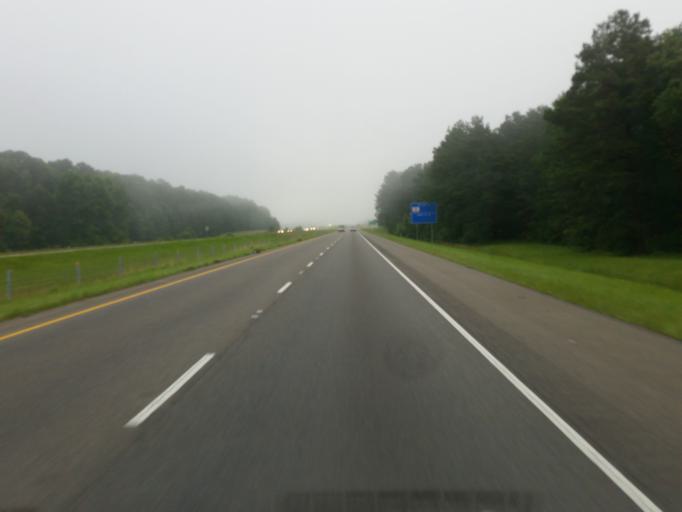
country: US
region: Louisiana
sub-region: Bossier Parish
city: Haughton
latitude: 32.5776
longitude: -93.4438
